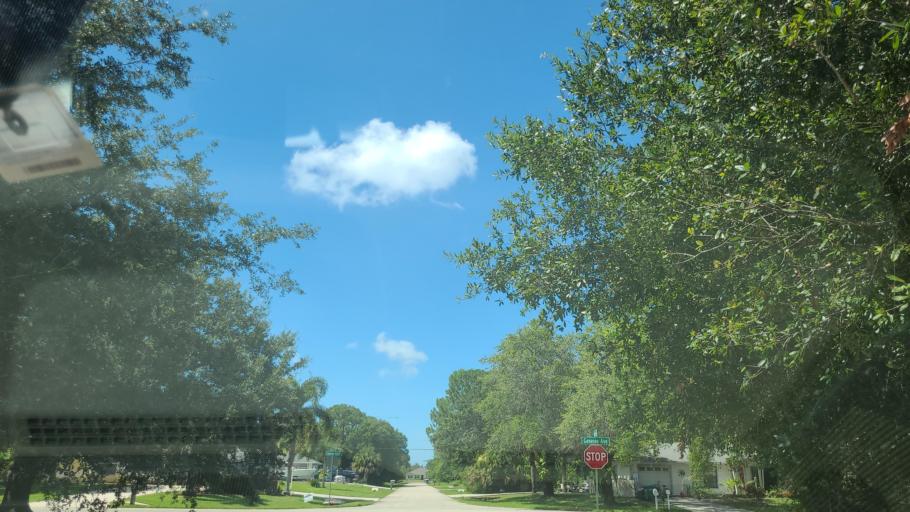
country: US
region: Florida
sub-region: Indian River County
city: Sebastian
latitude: 27.7703
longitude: -80.4957
